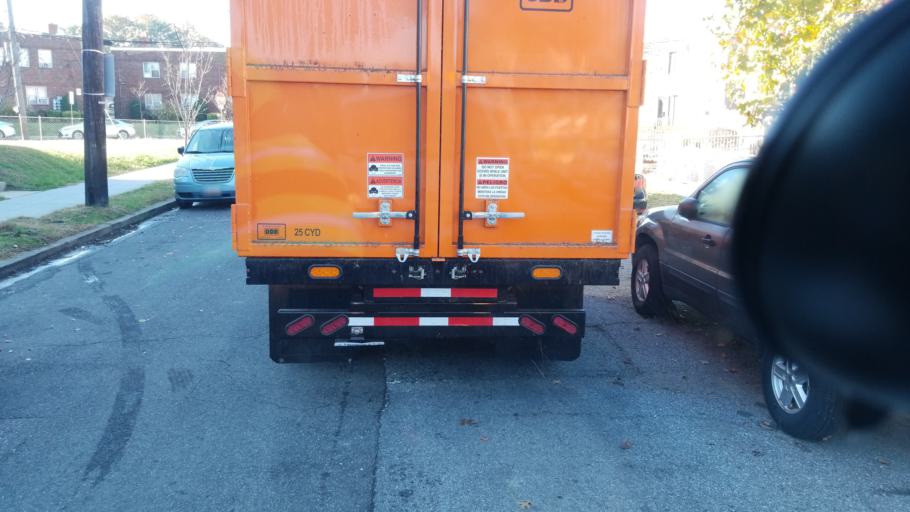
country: US
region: Maryland
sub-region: Prince George's County
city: Capitol Heights
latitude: 38.8911
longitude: -76.9548
